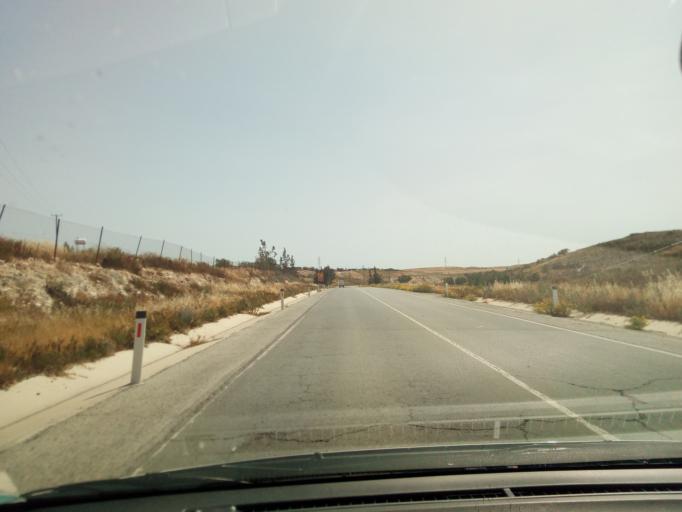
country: CY
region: Larnaka
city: Athienou
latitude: 35.0360
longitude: 33.5528
